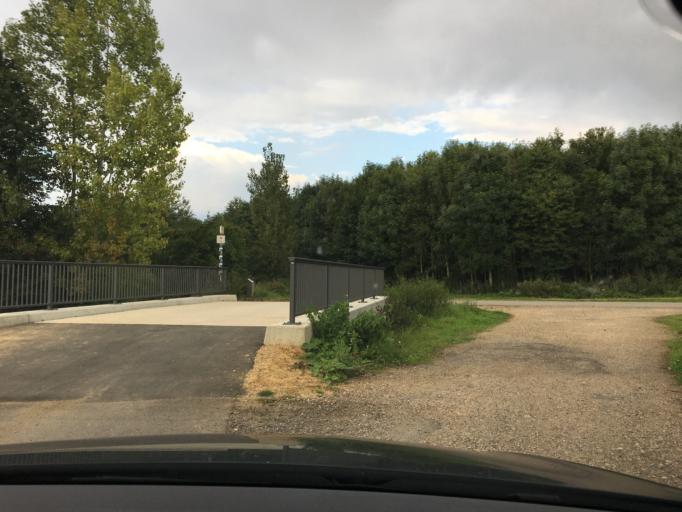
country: DE
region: North Rhine-Westphalia
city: Tuernich
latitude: 50.8562
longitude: 6.7335
